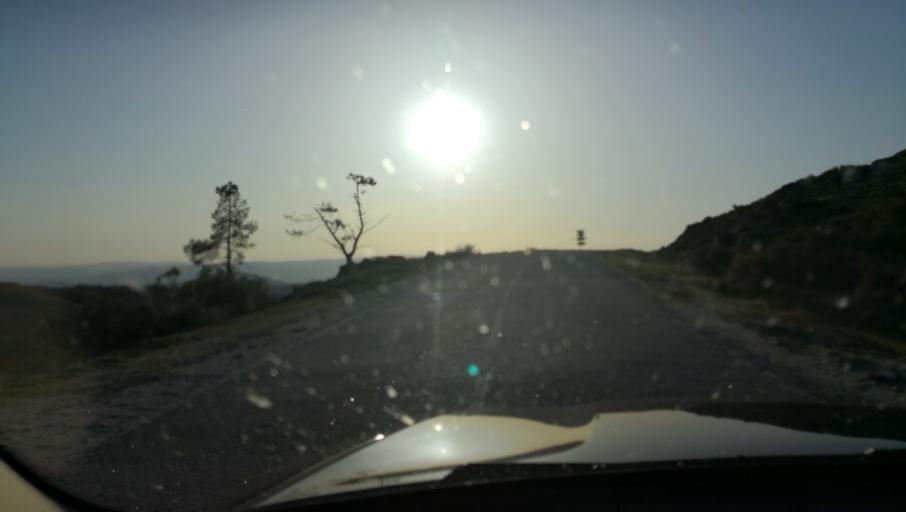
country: PT
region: Vila Real
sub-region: Vila Real
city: Vila Real
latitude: 41.3809
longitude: -7.8197
